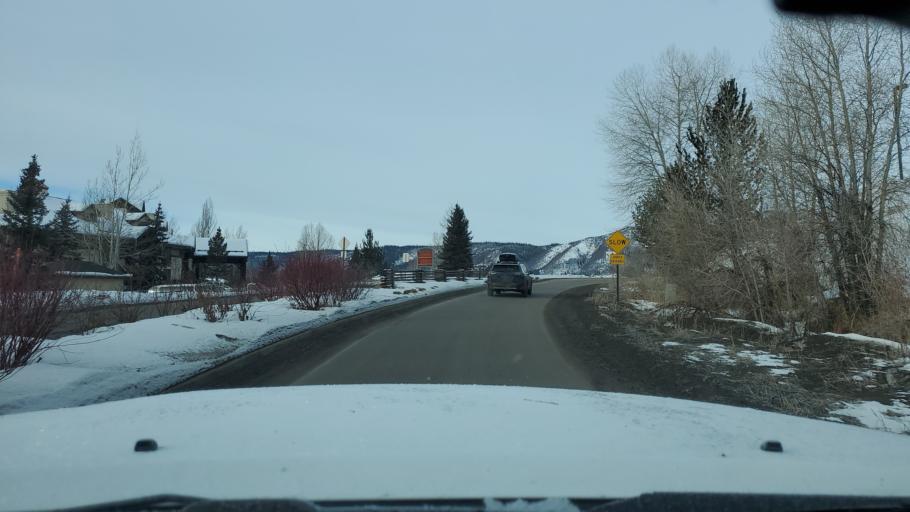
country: US
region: Colorado
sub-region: Routt County
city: Steamboat Springs
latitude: 40.4552
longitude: -106.8068
